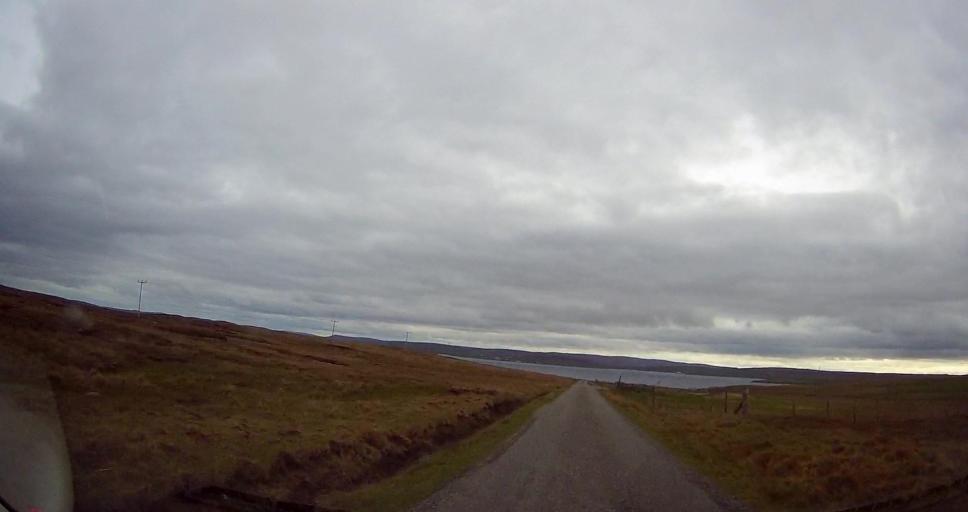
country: GB
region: Scotland
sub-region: Shetland Islands
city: Shetland
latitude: 60.5050
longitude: -1.1460
